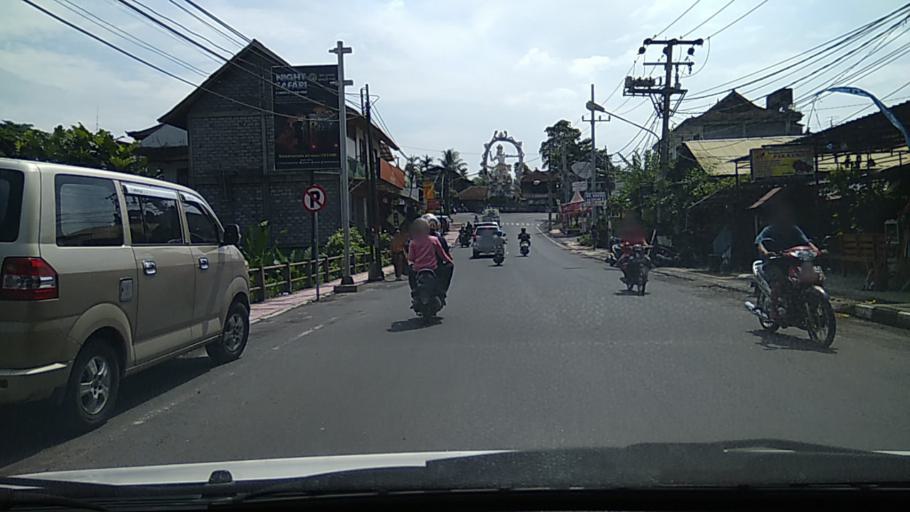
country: ID
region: Bali
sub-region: Kabupaten Gianyar
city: Ubud
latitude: -8.5091
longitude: 115.2703
